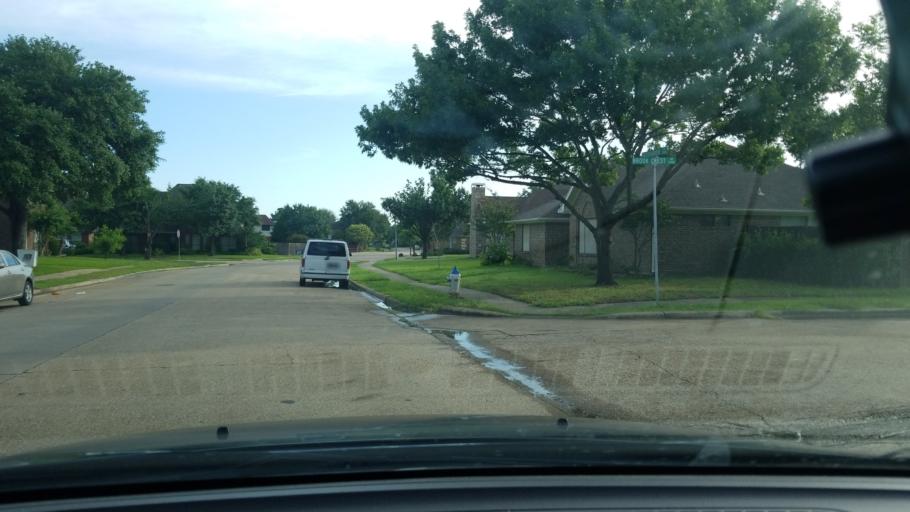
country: US
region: Texas
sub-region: Dallas County
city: Mesquite
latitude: 32.7981
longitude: -96.6026
